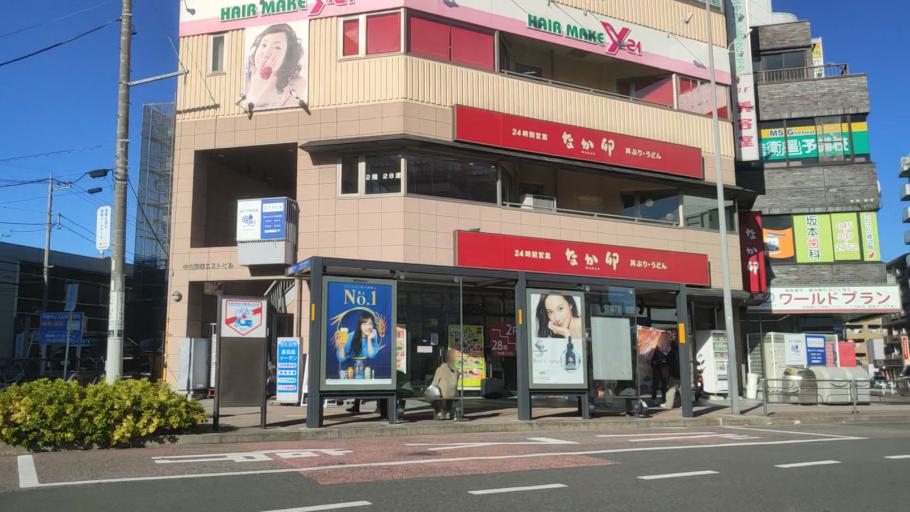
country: JP
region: Tokyo
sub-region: Machida-shi
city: Machida
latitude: 35.5150
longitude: 139.5401
